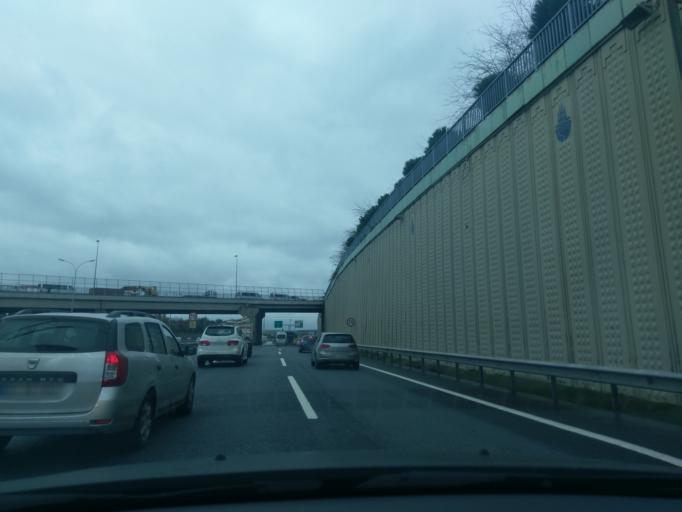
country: TR
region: Istanbul
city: Sisli
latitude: 41.1012
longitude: 28.9997
